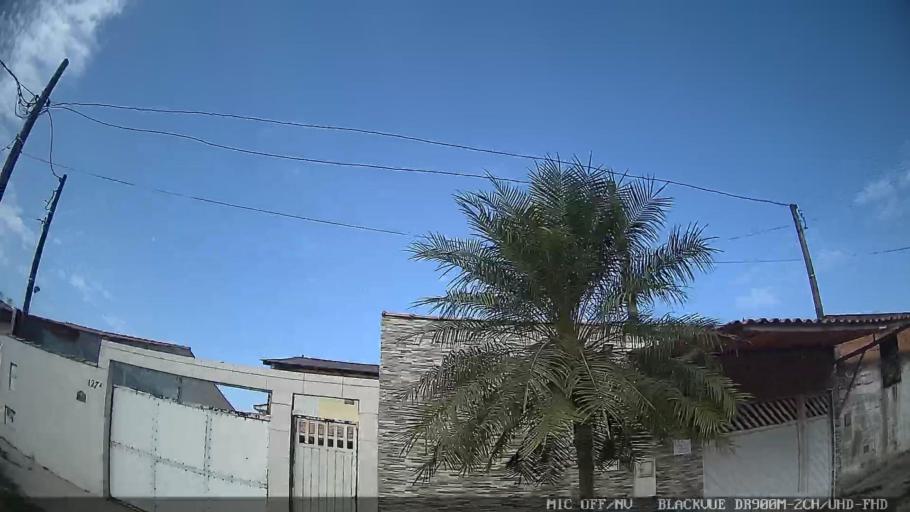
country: BR
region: Sao Paulo
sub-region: Guaruja
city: Guaruja
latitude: -23.9759
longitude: -46.2138
